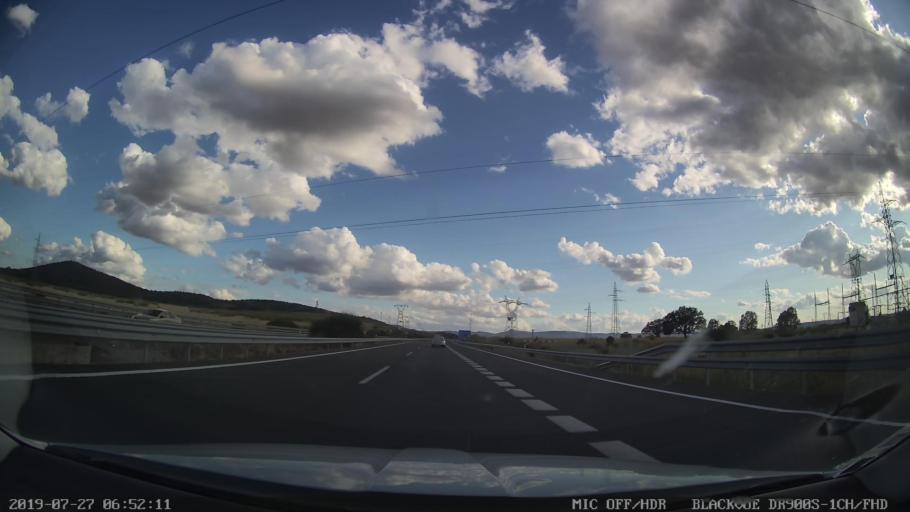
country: ES
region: Extremadura
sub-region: Provincia de Caceres
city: Almaraz
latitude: 39.8206
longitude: -5.6618
